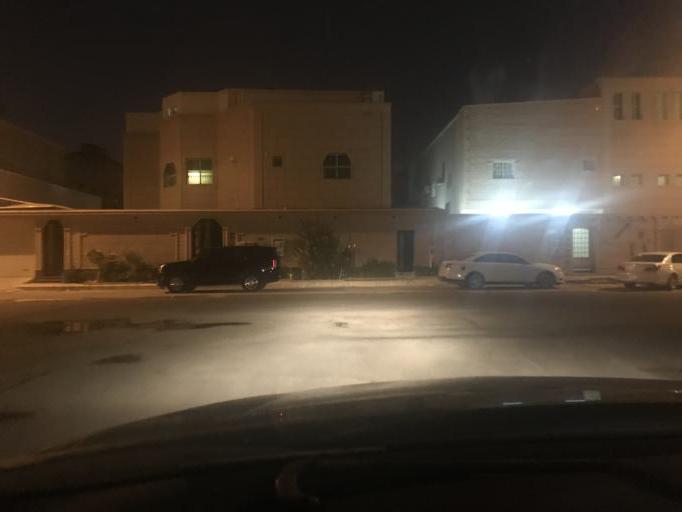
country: SA
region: Ar Riyad
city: Riyadh
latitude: 24.7389
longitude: 46.7865
